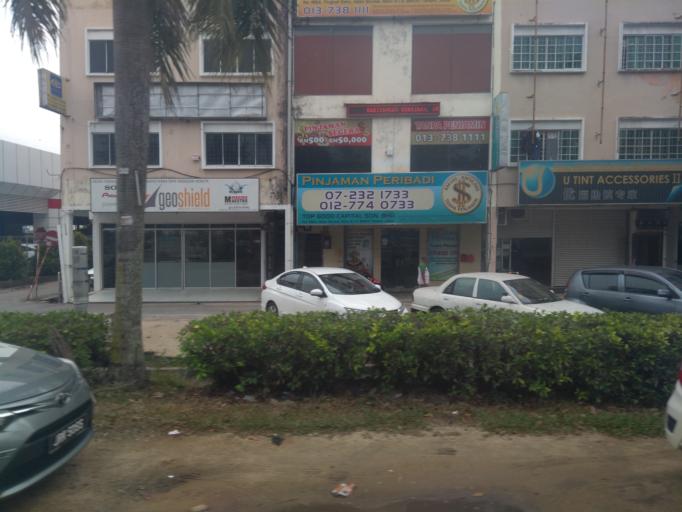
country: MY
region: Johor
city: Johor Bahru
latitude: 1.4892
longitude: 103.7119
